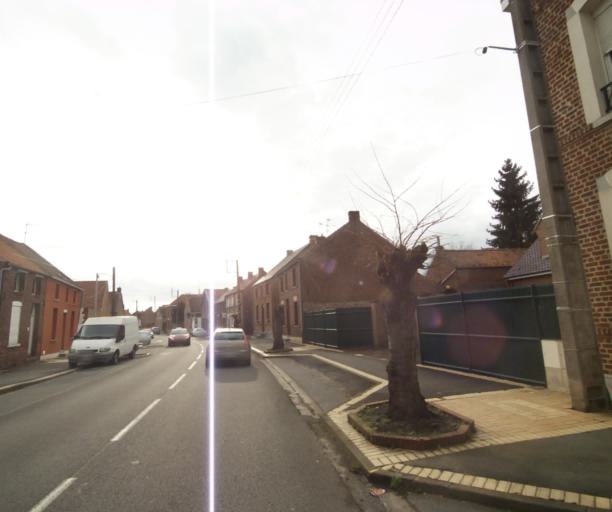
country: FR
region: Nord-Pas-de-Calais
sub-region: Departement du Nord
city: Quarouble
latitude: 50.3927
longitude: 3.6192
